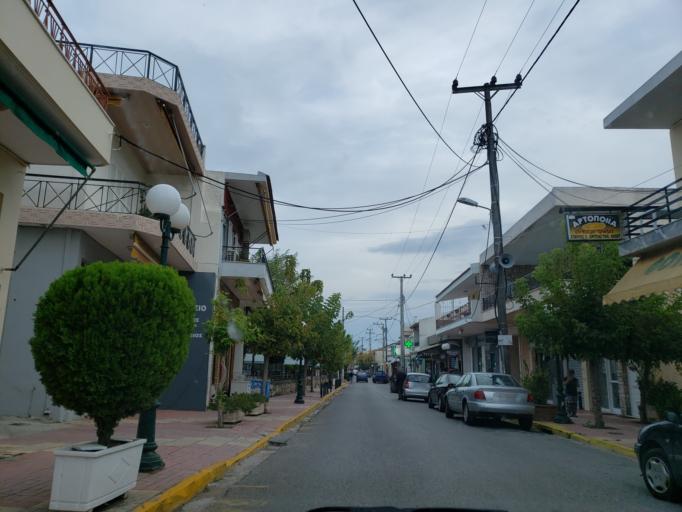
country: GR
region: Attica
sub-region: Nomarchia Anatolikis Attikis
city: Marathonas
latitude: 38.1577
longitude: 23.9593
